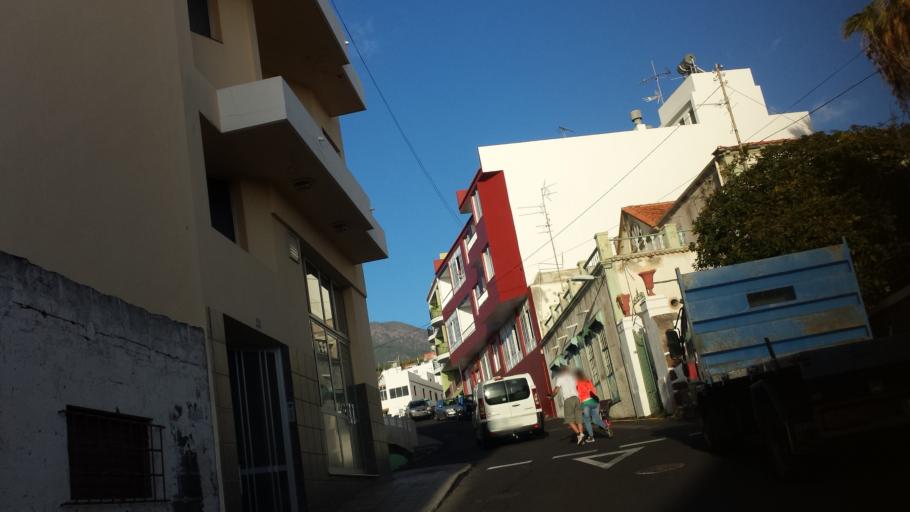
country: ES
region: Canary Islands
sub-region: Provincia de Santa Cruz de Tenerife
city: Tazacorte
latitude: 28.6420
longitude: -17.9331
